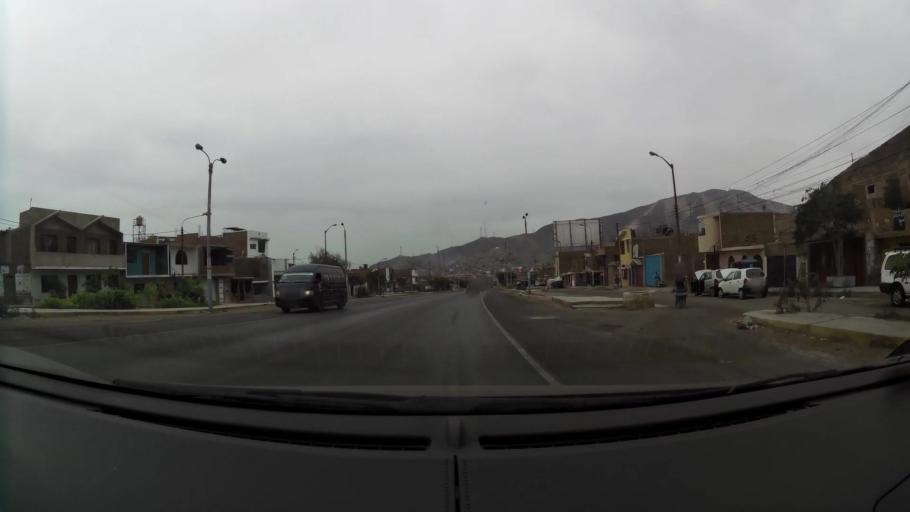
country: PE
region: Ancash
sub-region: Provincia de Santa
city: Coishco
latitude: -9.0278
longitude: -78.6162
